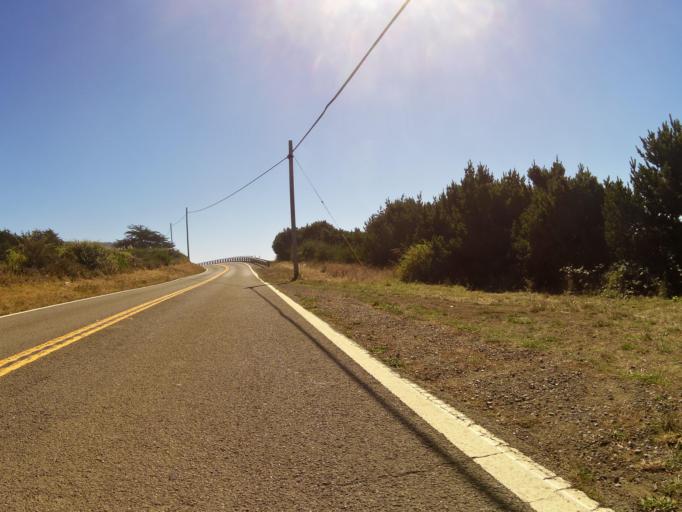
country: US
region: California
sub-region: Mendocino County
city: Fort Bragg
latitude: 39.6544
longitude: -123.7845
